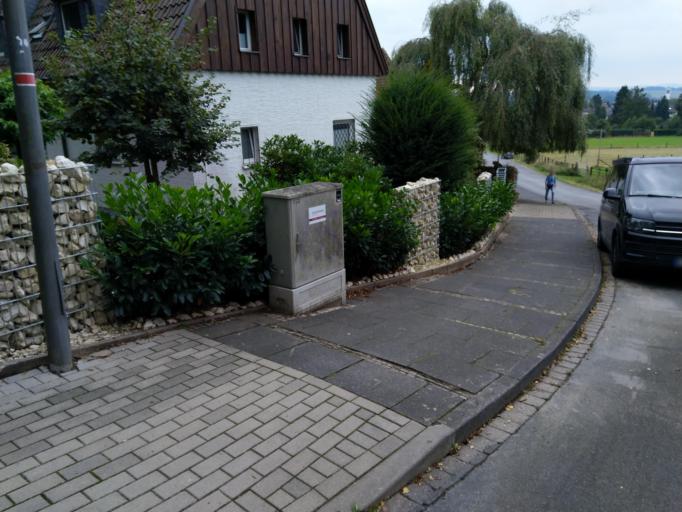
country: DE
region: North Rhine-Westphalia
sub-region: Regierungsbezirk Detmold
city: Bad Salzuflen
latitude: 52.0856
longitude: 8.7686
